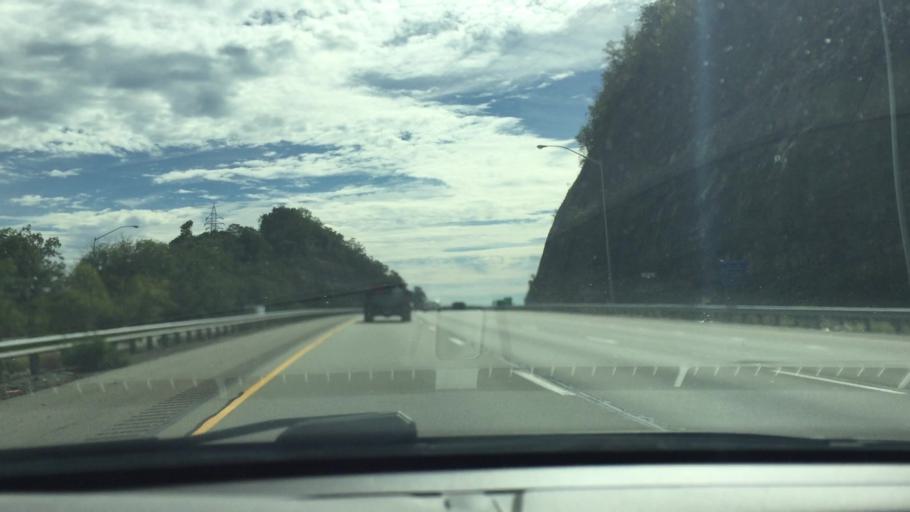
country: US
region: Pennsylvania
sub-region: Allegheny County
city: Heidelberg
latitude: 40.3945
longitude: -80.1019
